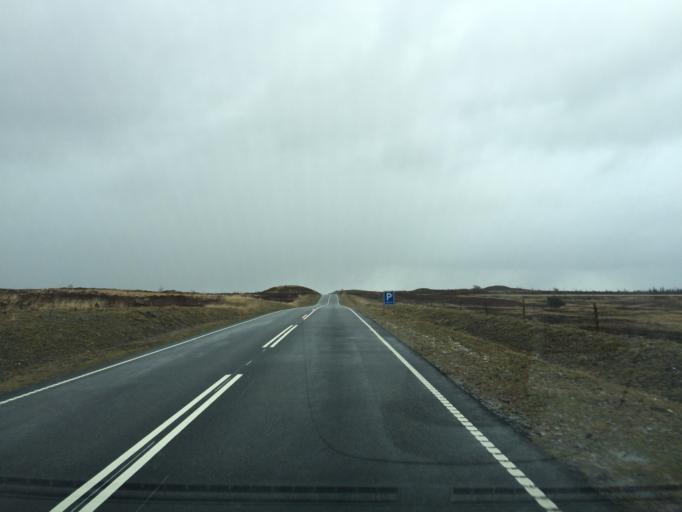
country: DK
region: Central Jutland
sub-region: Ringkobing-Skjern Kommune
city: Videbaek
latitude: 56.1830
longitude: 8.6592
